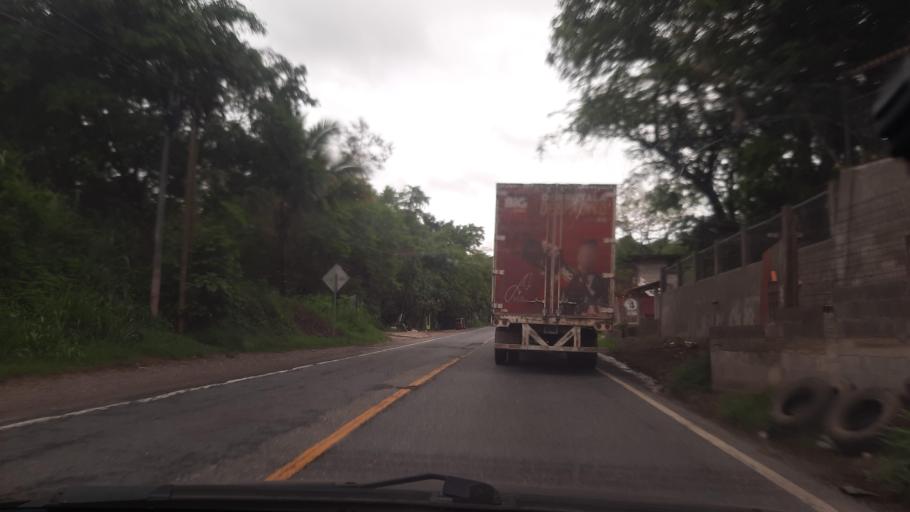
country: GT
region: Izabal
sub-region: Municipio de Los Amates
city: Los Amates
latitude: 15.2775
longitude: -89.0735
